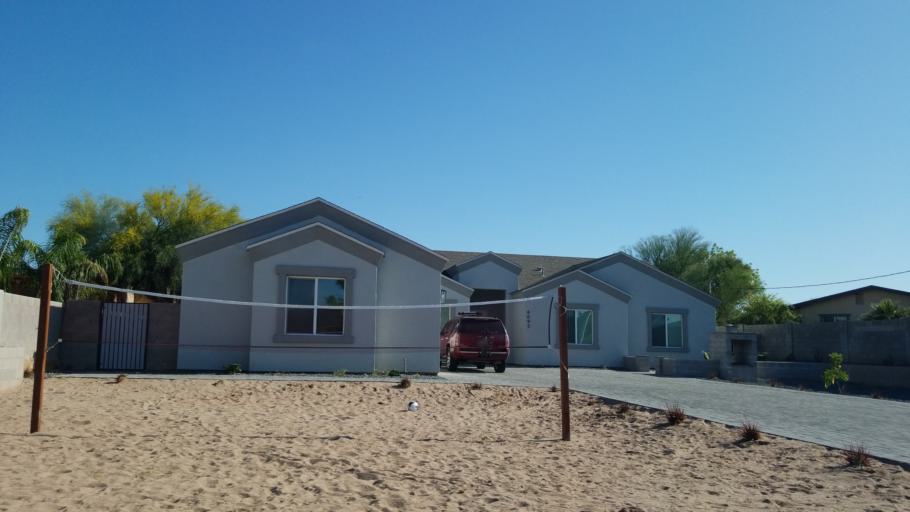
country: US
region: Arizona
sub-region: Maricopa County
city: Paradise Valley
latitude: 33.6227
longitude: -111.9940
